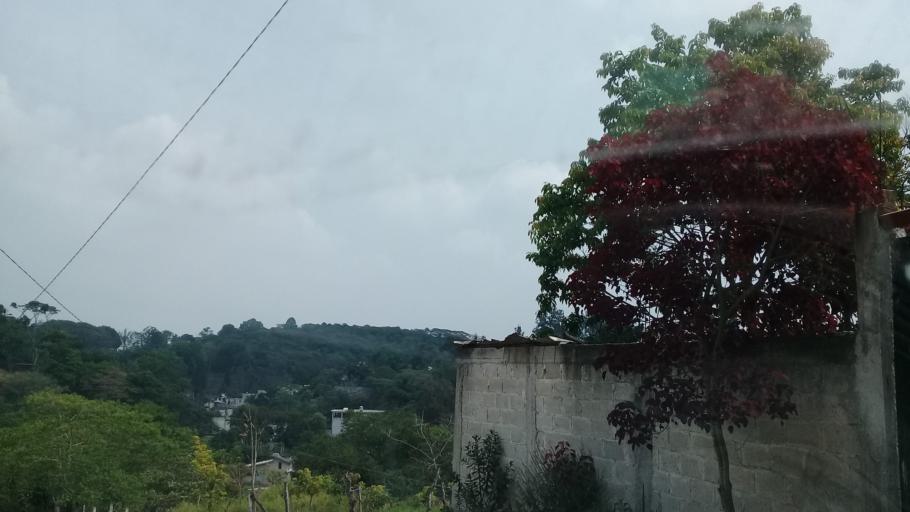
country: MX
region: Veracruz
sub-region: Xalapa
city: Fraccionamiento las Fuentes
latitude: 19.4922
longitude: -96.8984
